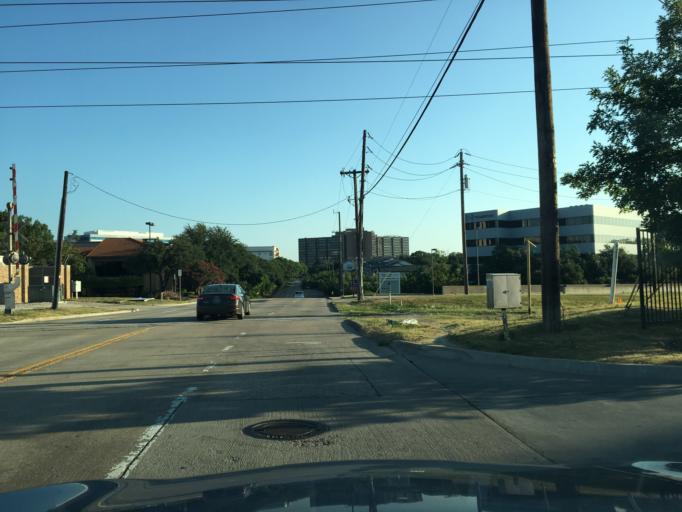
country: US
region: Texas
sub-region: Dallas County
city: Addison
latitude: 32.9621
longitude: -96.8189
